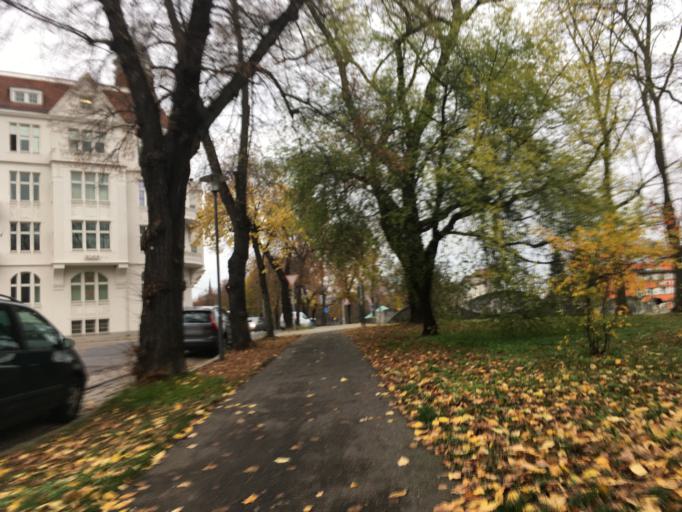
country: DE
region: Brandenburg
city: Frankfurt (Oder)
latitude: 52.3331
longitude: 14.5537
